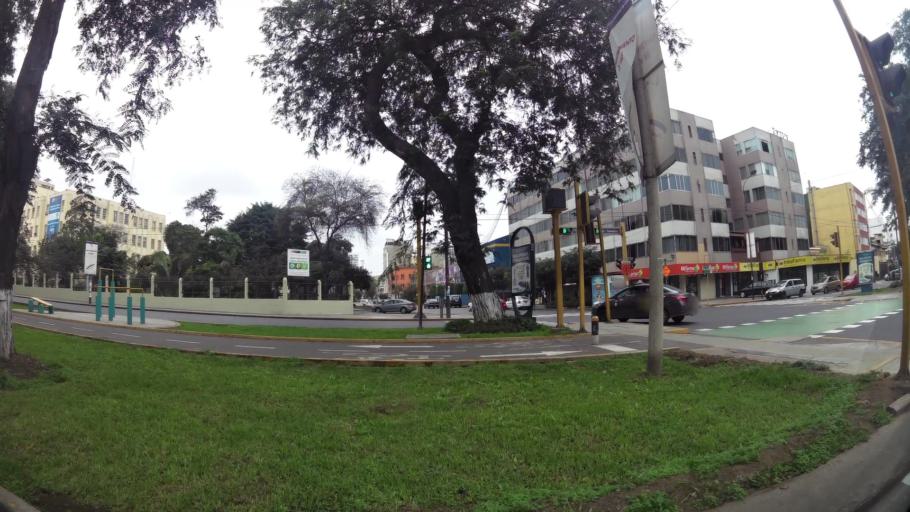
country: PE
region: Lima
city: Lima
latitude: -12.0737
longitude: -77.0420
